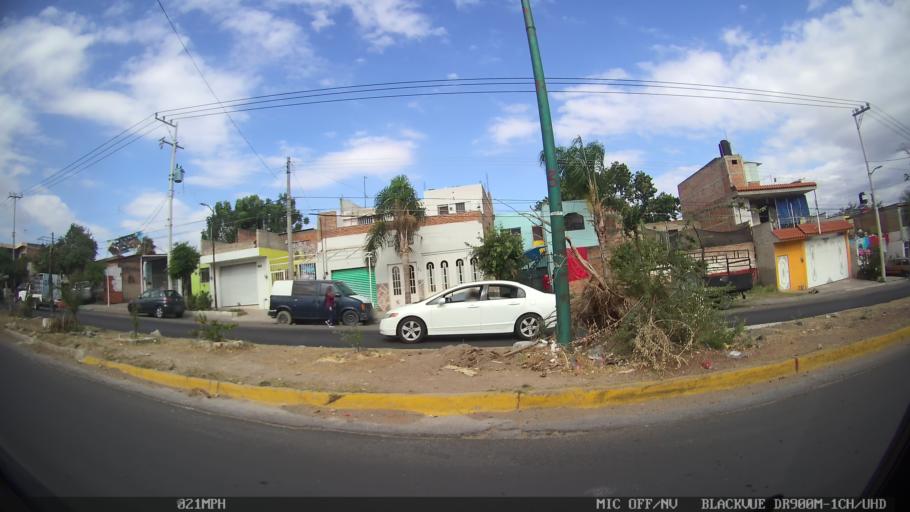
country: MX
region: Jalisco
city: Tlaquepaque
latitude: 20.6851
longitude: -103.2586
